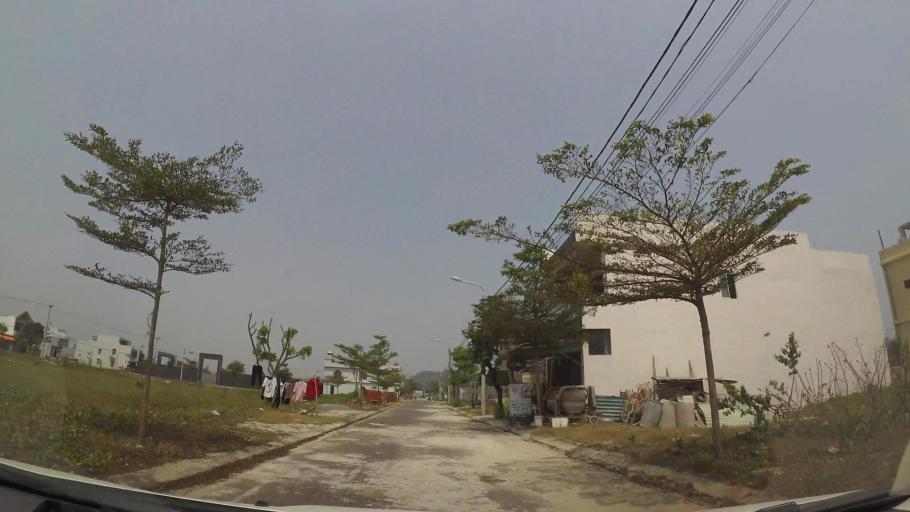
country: VN
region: Da Nang
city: Ngu Hanh Son
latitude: 15.9867
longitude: 108.2618
